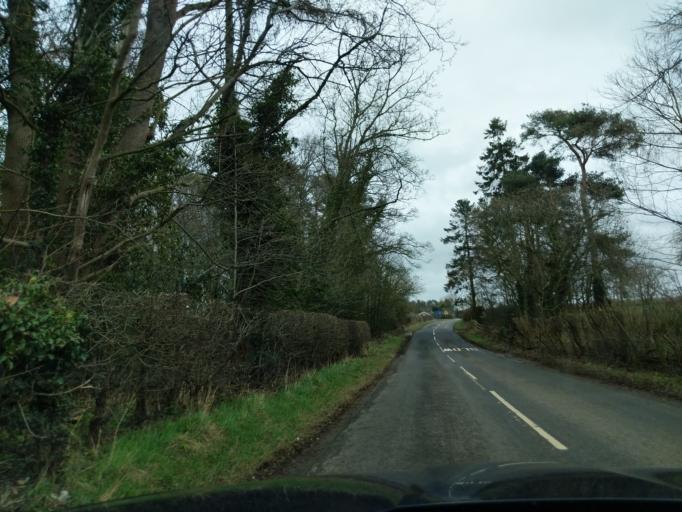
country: GB
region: England
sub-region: Northumberland
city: Morpeth
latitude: 55.1804
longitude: -1.7240
